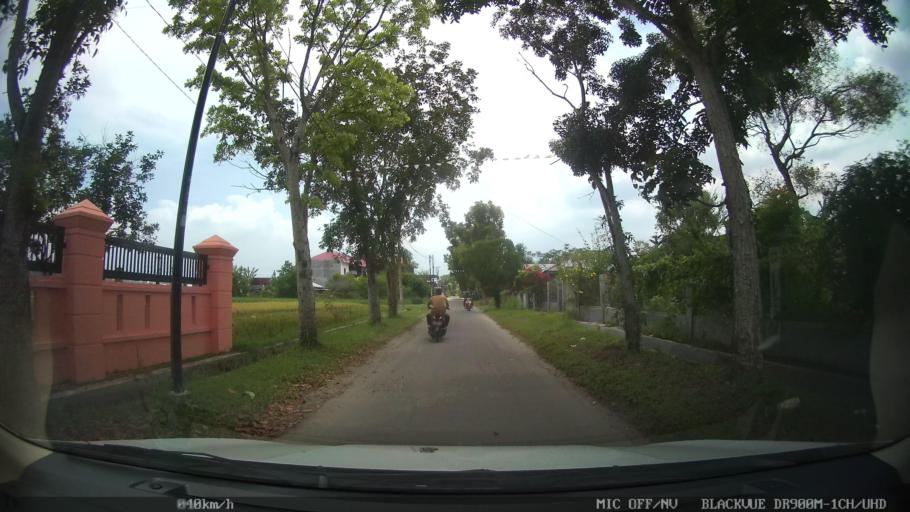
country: ID
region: North Sumatra
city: Binjai
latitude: 3.6207
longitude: 98.5118
